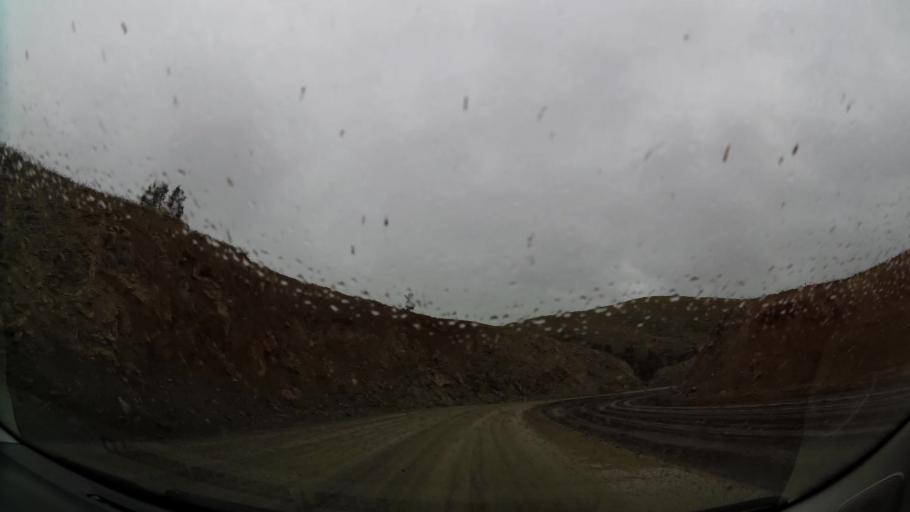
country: MA
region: Taza-Al Hoceima-Taounate
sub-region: Taza
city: Ajdir
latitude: 34.9023
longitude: -3.7873
